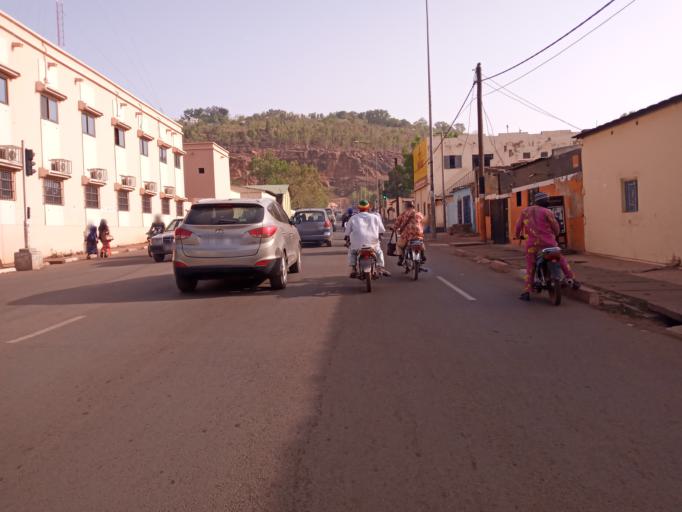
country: ML
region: Bamako
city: Bamako
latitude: 12.6525
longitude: -8.0076
